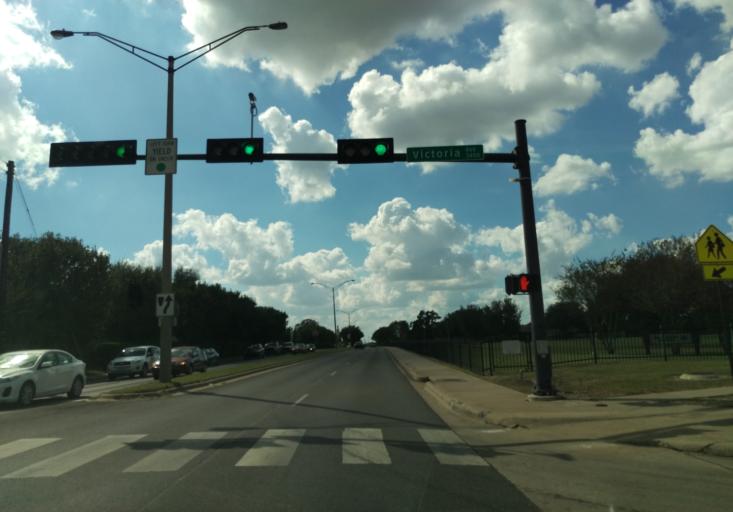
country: US
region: Texas
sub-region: Brazos County
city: College Station
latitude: 30.5752
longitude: -96.3048
